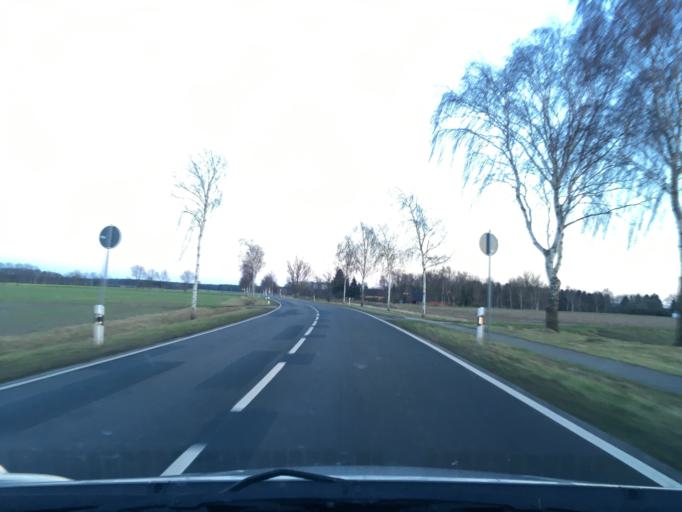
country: DE
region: Lower Saxony
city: Waddeweitz
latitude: 52.9872
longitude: 10.9832
